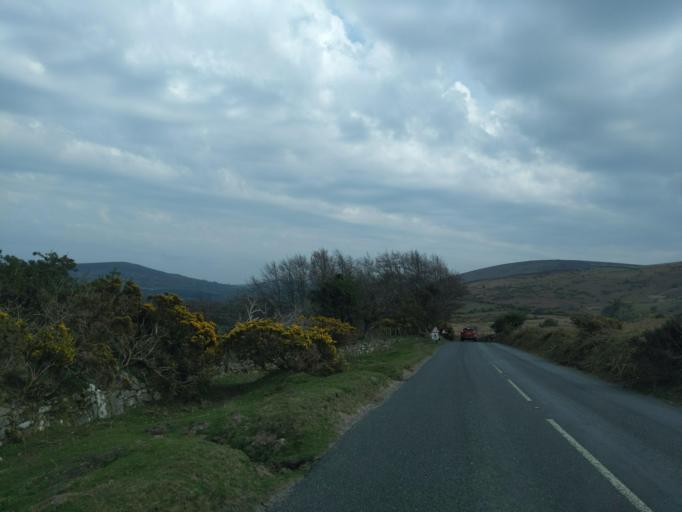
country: GB
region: England
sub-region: Devon
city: Ashburton
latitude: 50.6356
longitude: -3.8407
